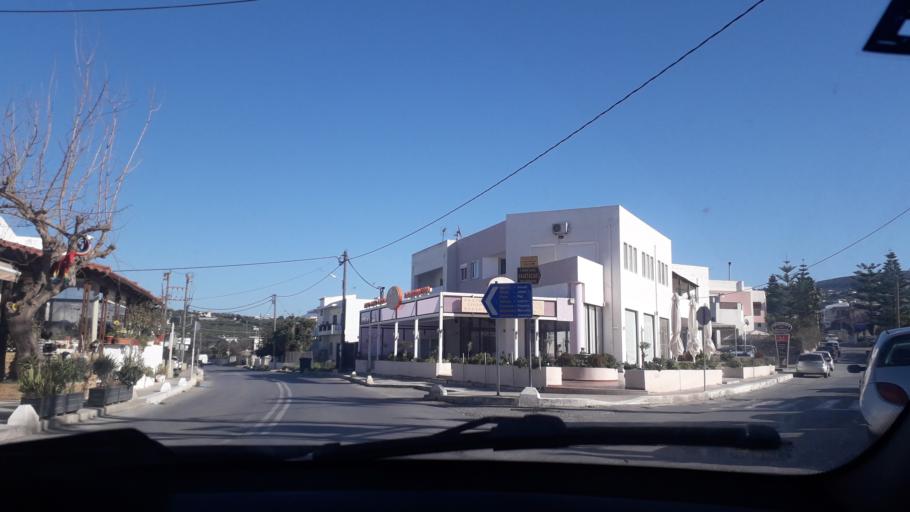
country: GR
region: Crete
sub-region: Nomos Rethymnis
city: Rethymno
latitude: 35.3668
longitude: 24.5347
